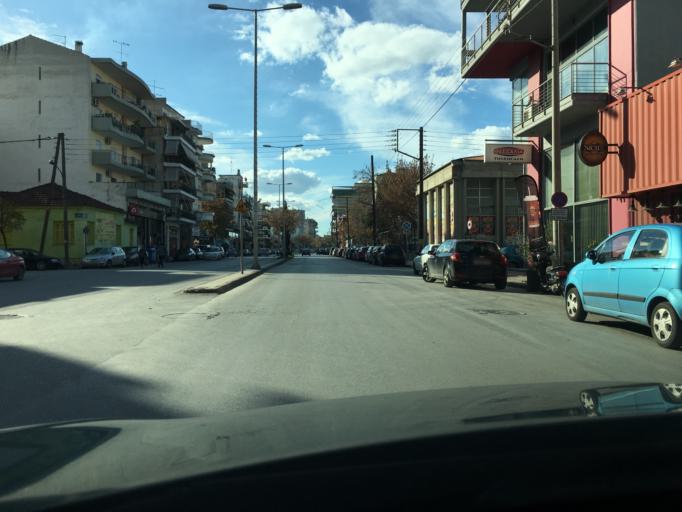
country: GR
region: Thessaly
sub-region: Nomos Larisis
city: Larisa
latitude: 39.6324
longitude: 22.4254
